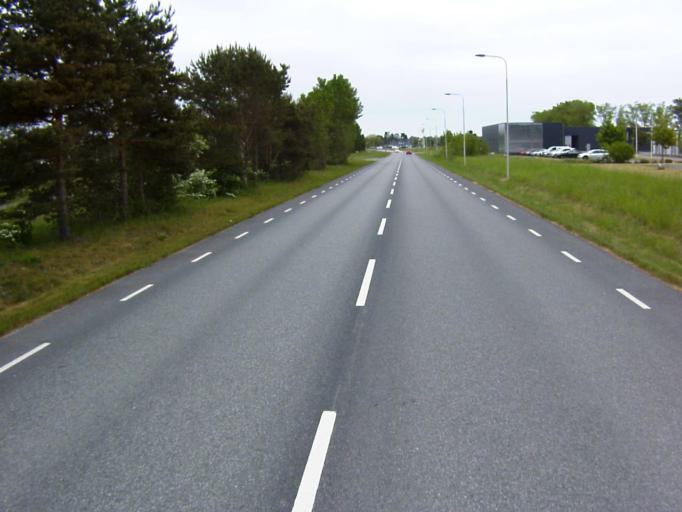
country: SE
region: Skane
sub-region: Kristianstads Kommun
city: Ahus
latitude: 55.9346
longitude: 14.2822
